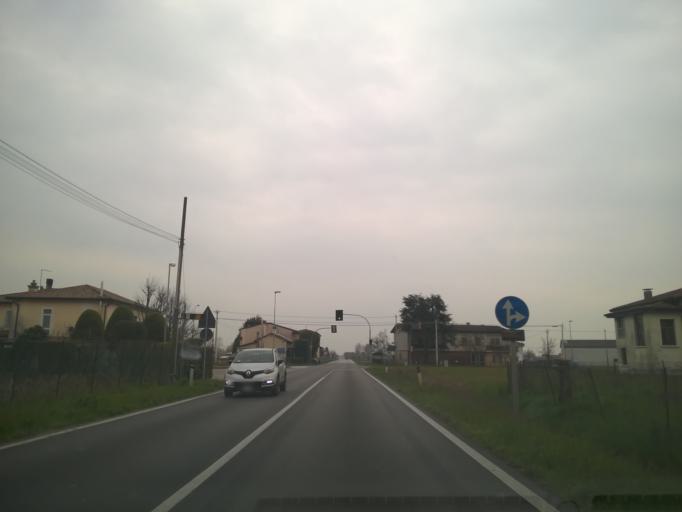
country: IT
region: Veneto
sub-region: Provincia di Padova
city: Grantorto
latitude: 45.5976
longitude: 11.7206
